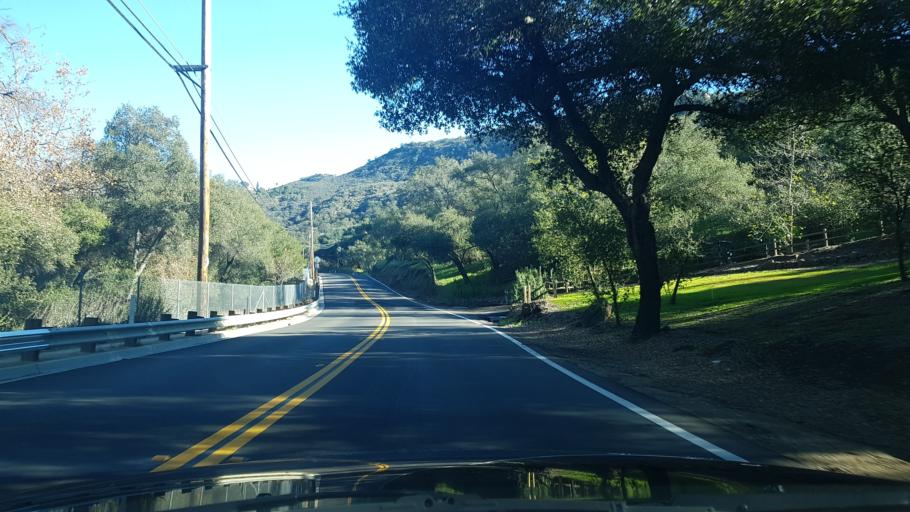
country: US
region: California
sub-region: San Diego County
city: Valley Center
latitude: 33.2055
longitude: -117.0090
